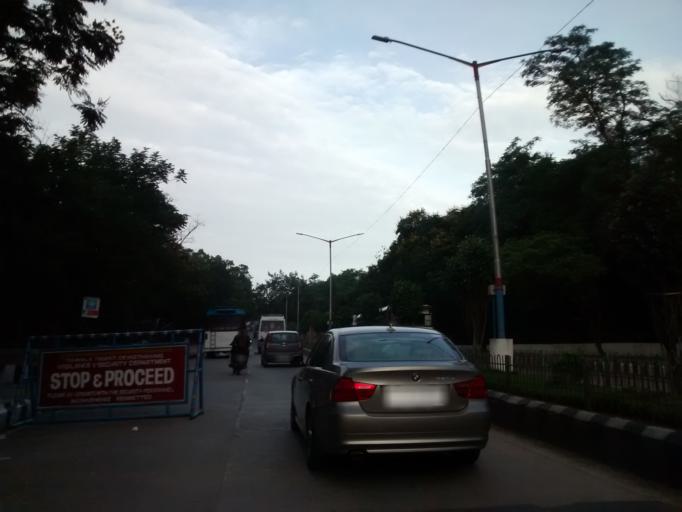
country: IN
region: Andhra Pradesh
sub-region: Chittoor
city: Akkarampalle
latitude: 13.6486
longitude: 79.4097
